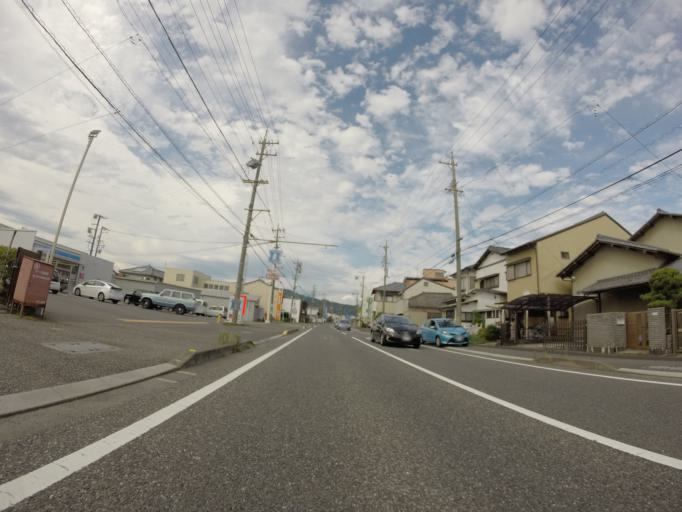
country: JP
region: Shizuoka
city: Shizuoka-shi
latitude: 35.0330
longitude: 138.4904
